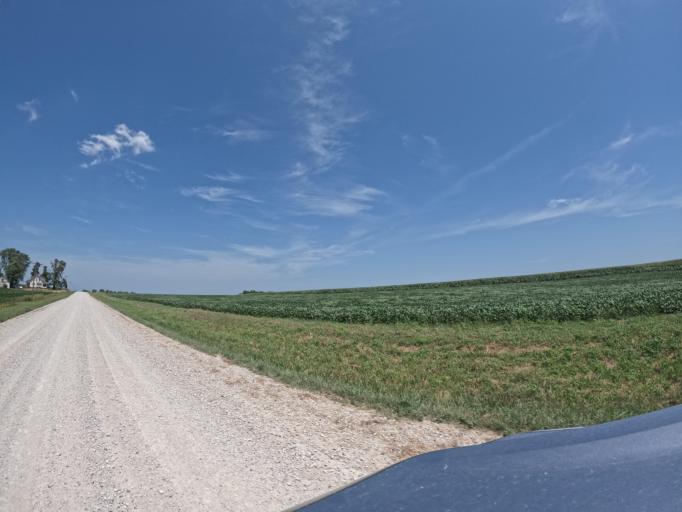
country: US
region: Iowa
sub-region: Henry County
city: Mount Pleasant
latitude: 40.9347
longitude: -91.6458
